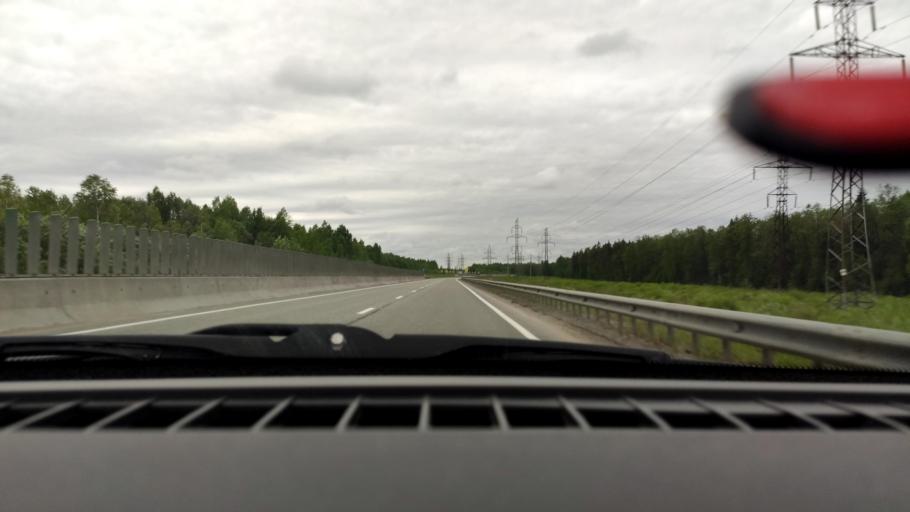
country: RU
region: Perm
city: Overyata
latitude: 58.0365
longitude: 55.9369
